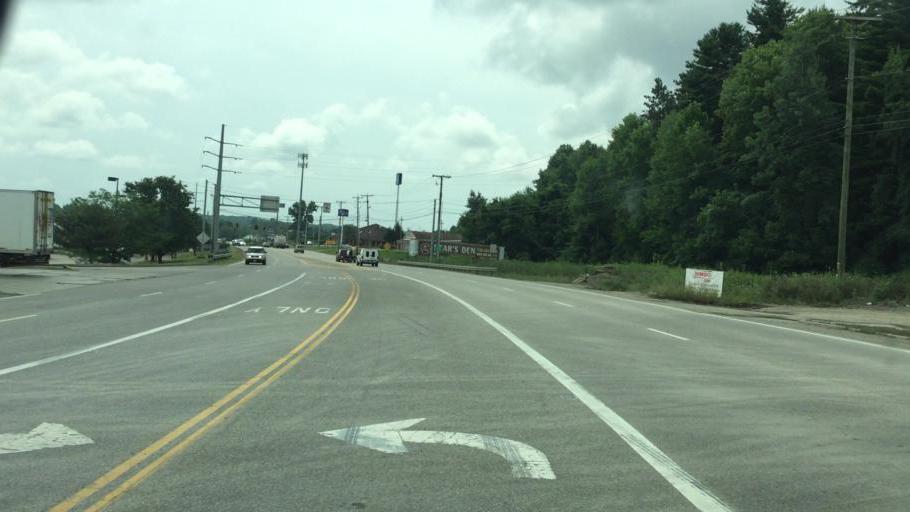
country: US
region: Ohio
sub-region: Guernsey County
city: Cambridge
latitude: 39.9969
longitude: -81.5777
